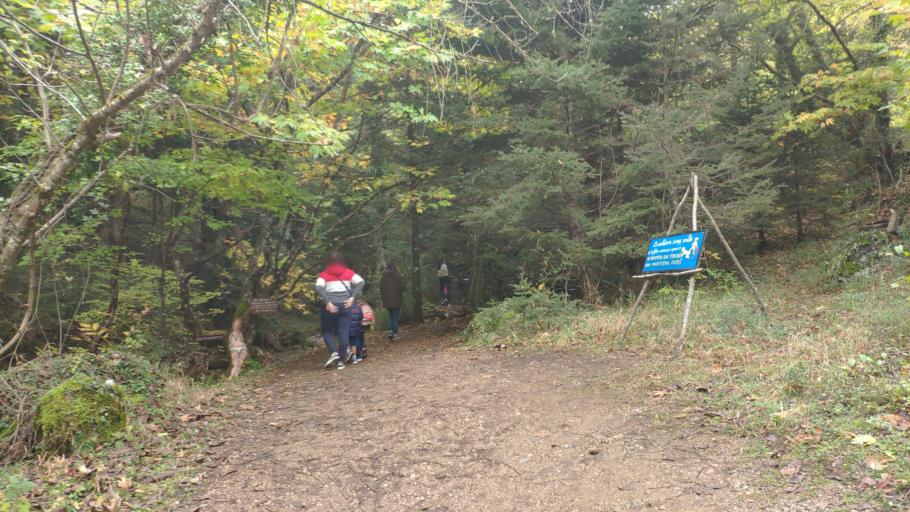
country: GR
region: Central Greece
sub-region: Nomos Fthiotidos
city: Stavros
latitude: 38.7369
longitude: 22.3382
